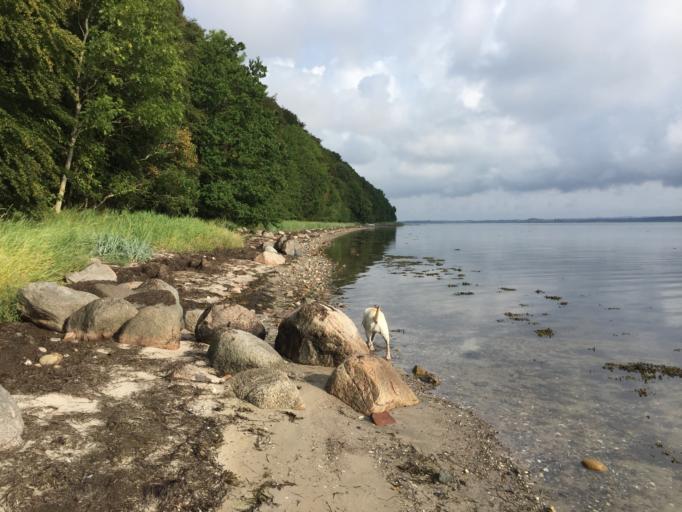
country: DK
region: South Denmark
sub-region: Assens Kommune
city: Harby
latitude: 55.1409
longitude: 10.0337
